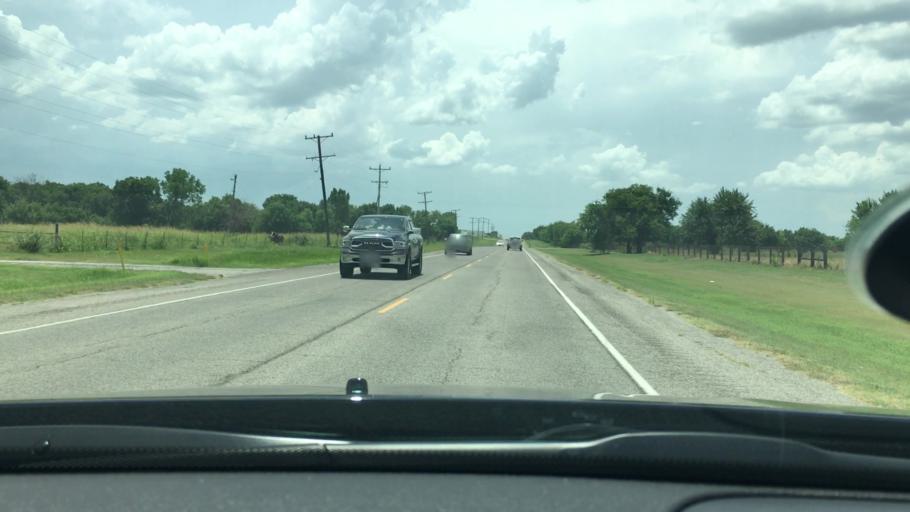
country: US
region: Oklahoma
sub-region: Love County
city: Marietta
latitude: 33.9562
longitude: -97.1263
